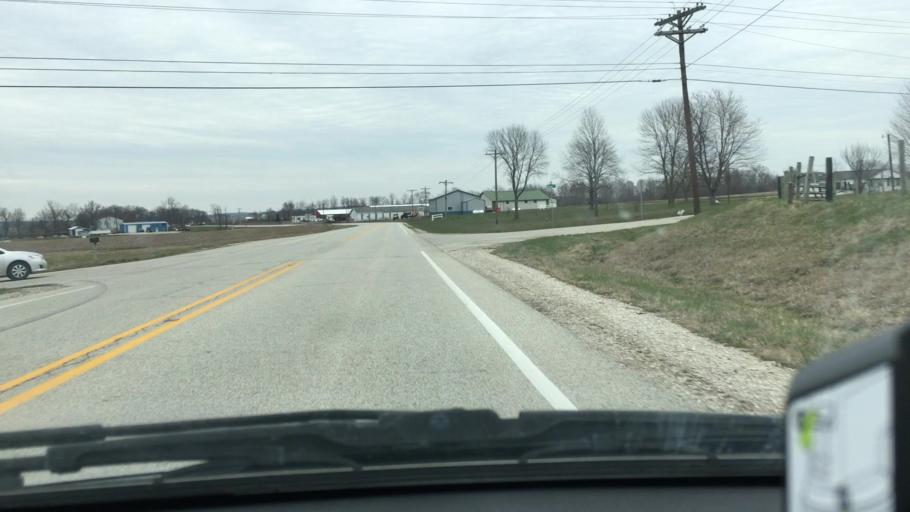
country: US
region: Indiana
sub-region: Greene County
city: Bloomfield
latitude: 39.0236
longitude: -87.0131
